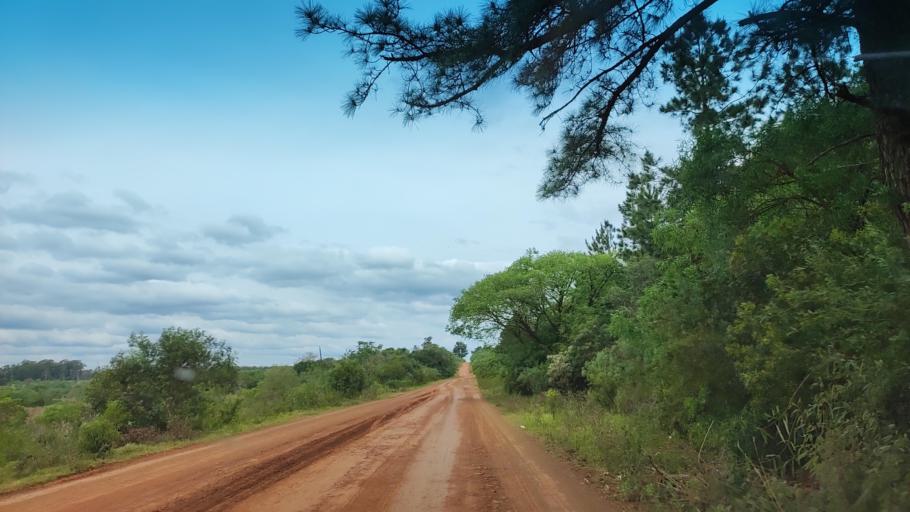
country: AR
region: Misiones
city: Garupa
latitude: -27.5183
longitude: -55.9748
